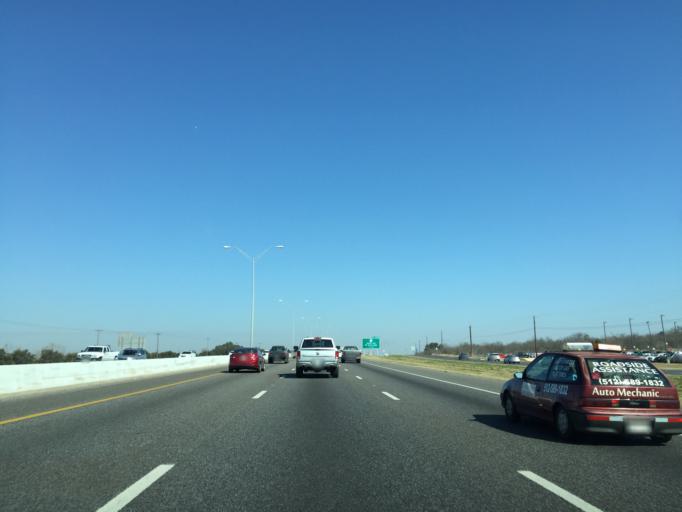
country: US
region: Texas
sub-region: Williamson County
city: Georgetown
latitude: 30.5827
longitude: -97.6928
